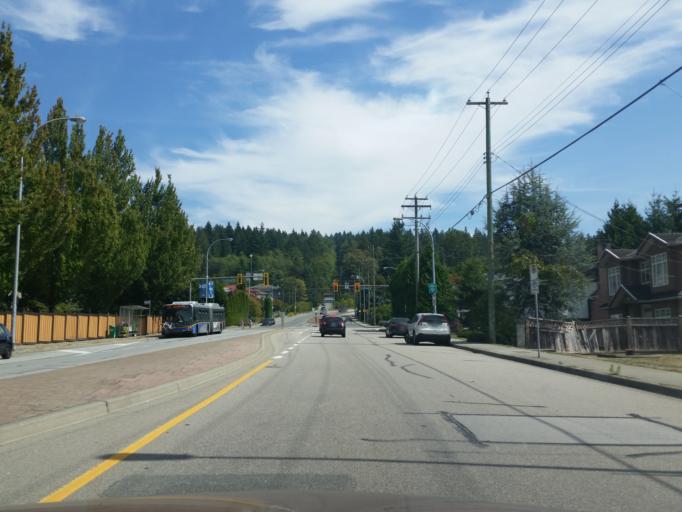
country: CA
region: British Columbia
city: Burnaby
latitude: 49.2804
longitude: -122.9549
